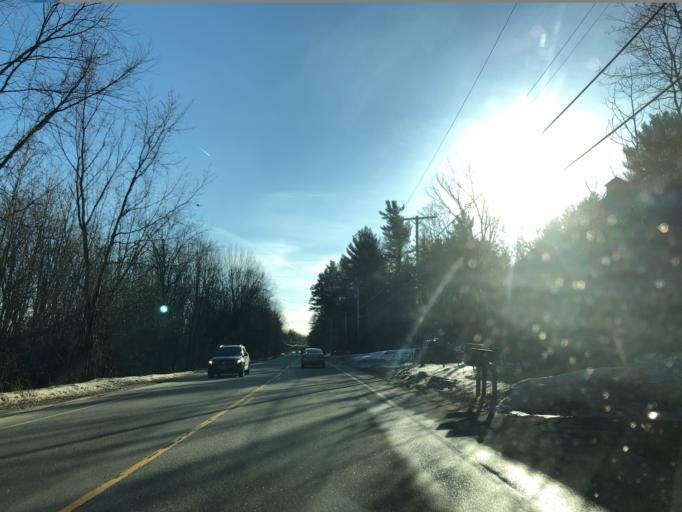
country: US
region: Maine
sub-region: Cumberland County
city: North Windham
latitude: 43.8682
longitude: -70.3658
